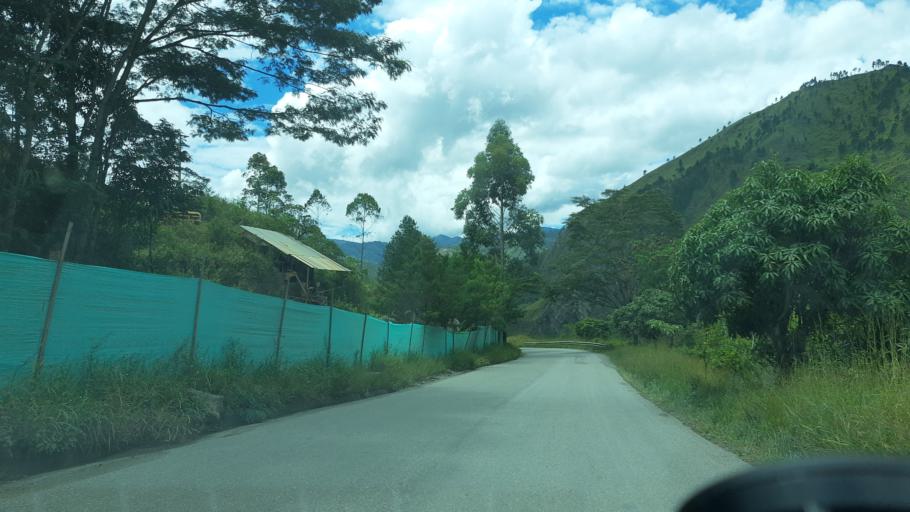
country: CO
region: Cundinamarca
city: Tenza
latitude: 5.0315
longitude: -73.3910
